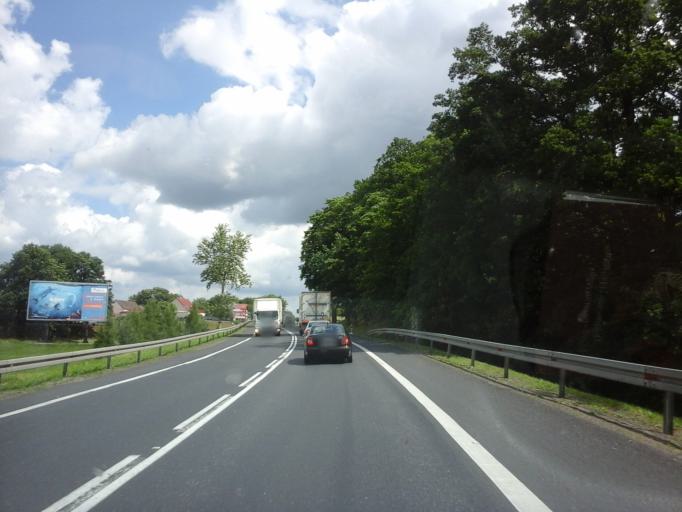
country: PL
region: West Pomeranian Voivodeship
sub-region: Powiat bialogardzki
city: Bialogard
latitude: 54.1243
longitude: 16.0155
